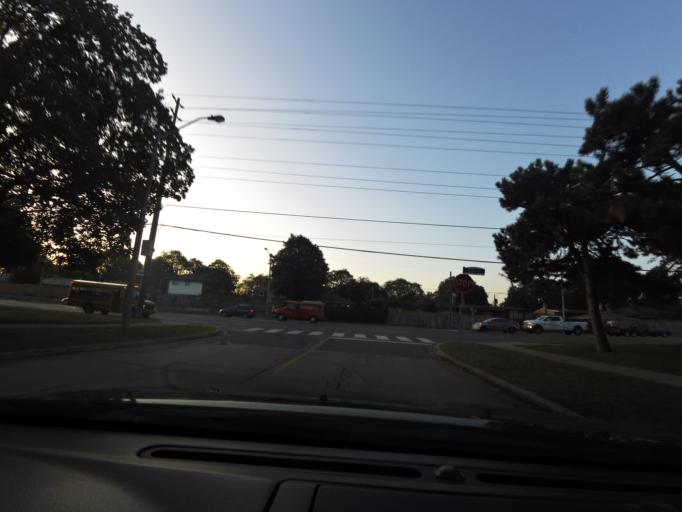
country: CA
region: Ontario
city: Etobicoke
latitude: 43.6934
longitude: -79.5642
